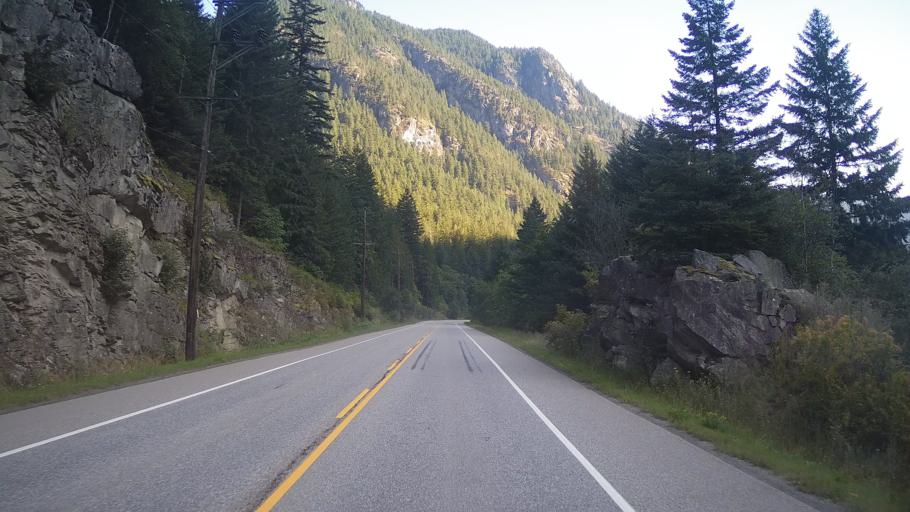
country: CA
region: British Columbia
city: Hope
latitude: 49.6064
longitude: -121.4155
